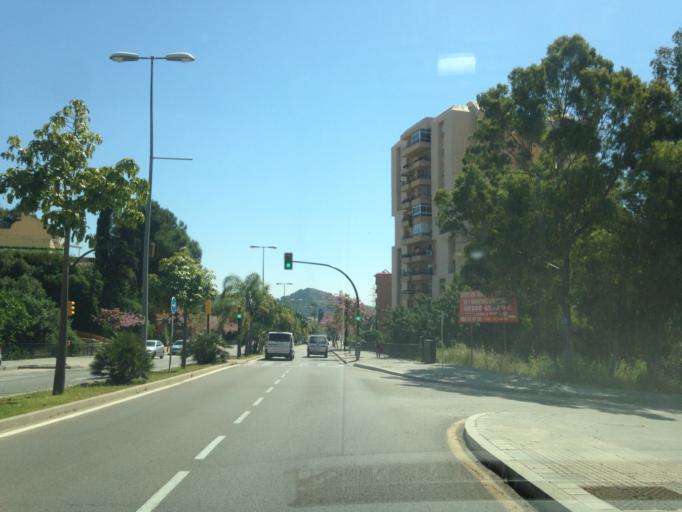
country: ES
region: Andalusia
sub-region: Provincia de Malaga
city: Malaga
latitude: 36.7325
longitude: -4.4733
